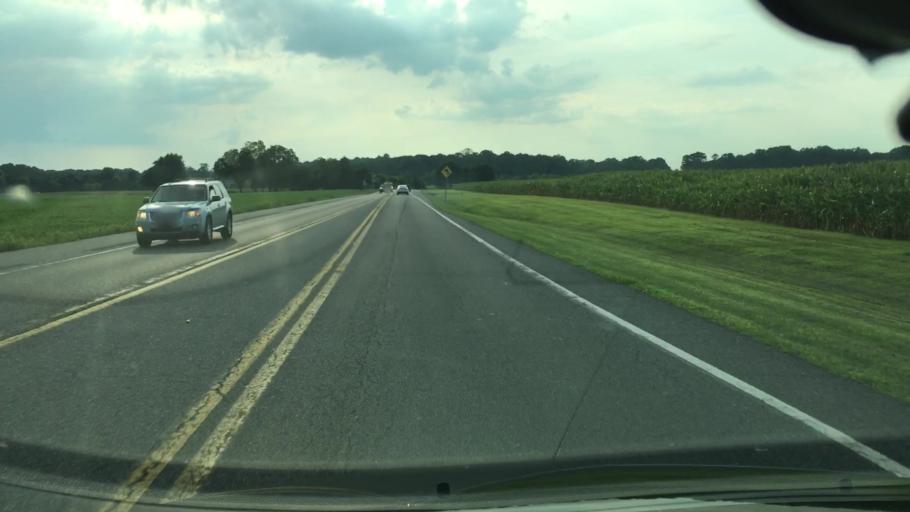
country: US
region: Maryland
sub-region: Worcester County
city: Ocean Pines
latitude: 38.3900
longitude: -75.1961
